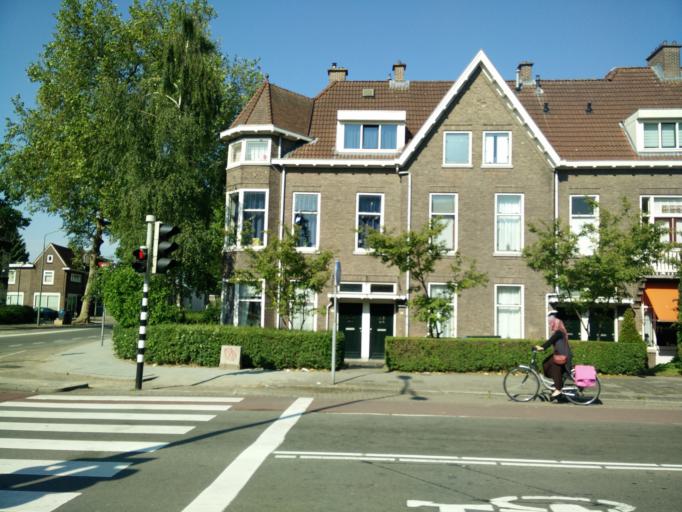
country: NL
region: South Holland
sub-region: Gemeente Dordrecht
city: Dordrecht
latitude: 51.8039
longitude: 4.6641
